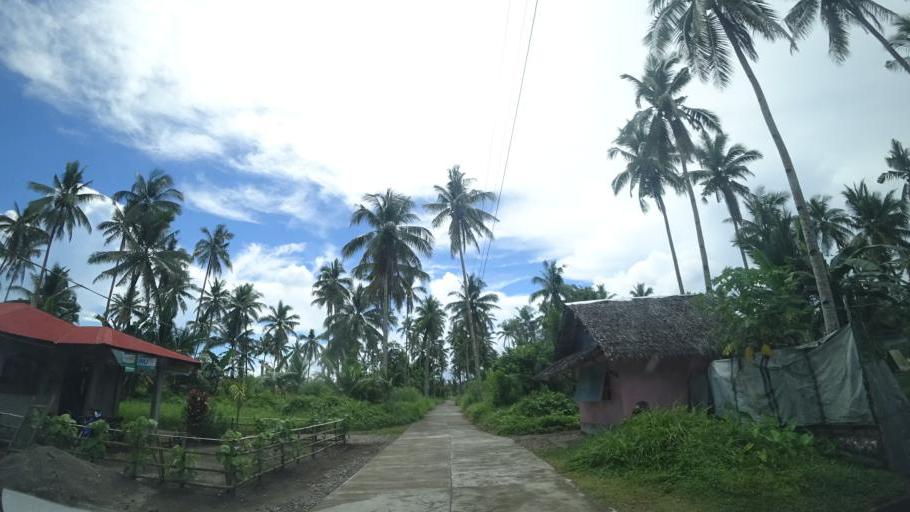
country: PH
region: Eastern Visayas
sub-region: Province of Leyte
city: Liberty
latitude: 10.8551
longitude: 125.0022
